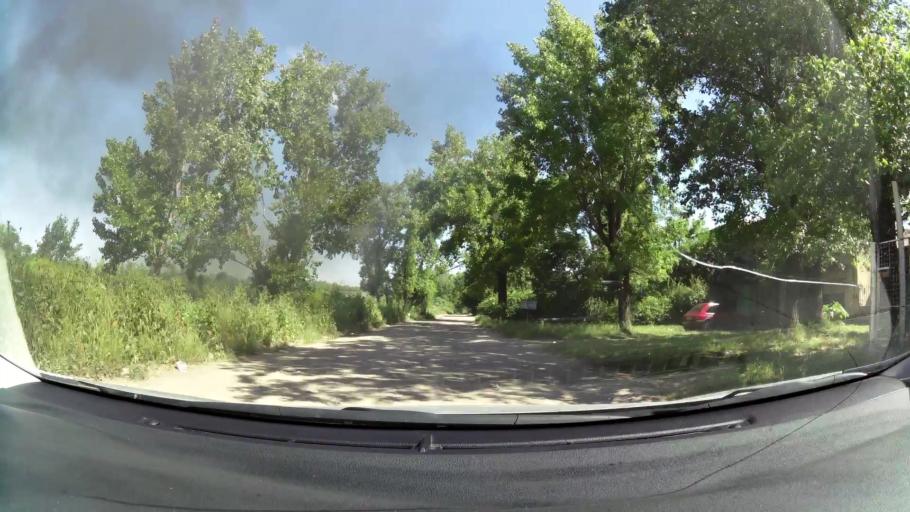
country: AR
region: Buenos Aires F.D.
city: Villa Lugano
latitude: -34.7007
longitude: -58.4706
